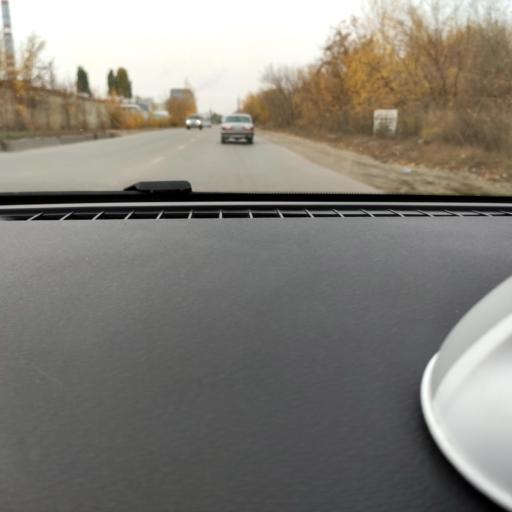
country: RU
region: Samara
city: Petra-Dubrava
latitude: 53.2568
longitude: 50.2834
